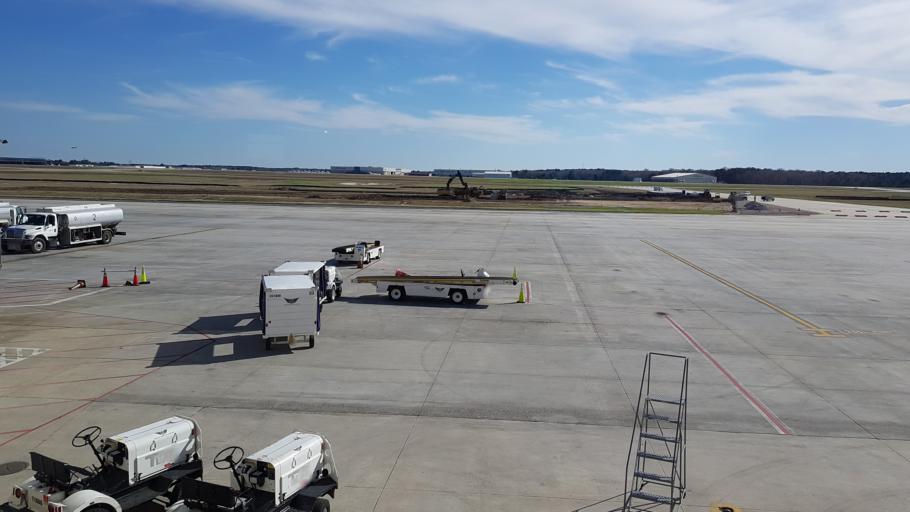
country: US
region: Georgia
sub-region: Chatham County
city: Pooler
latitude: 32.1356
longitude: -81.2072
